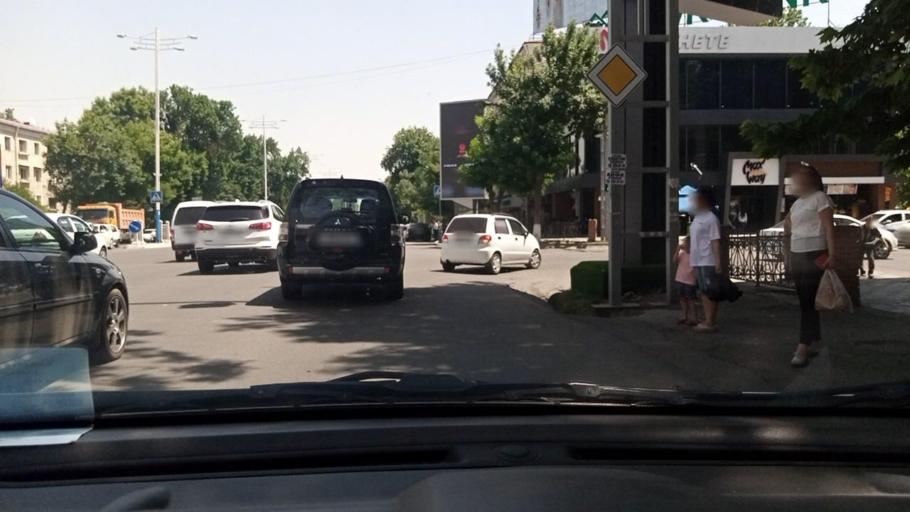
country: UZ
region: Toshkent Shahri
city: Tashkent
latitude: 41.2883
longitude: 69.2290
